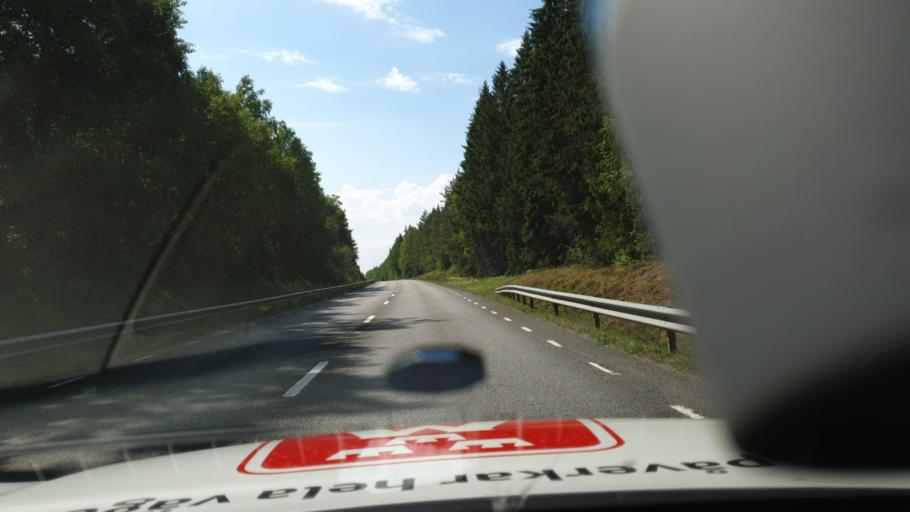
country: SE
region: Joenkoeping
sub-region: Habo Kommun
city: Habo
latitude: 57.9800
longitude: 14.1059
